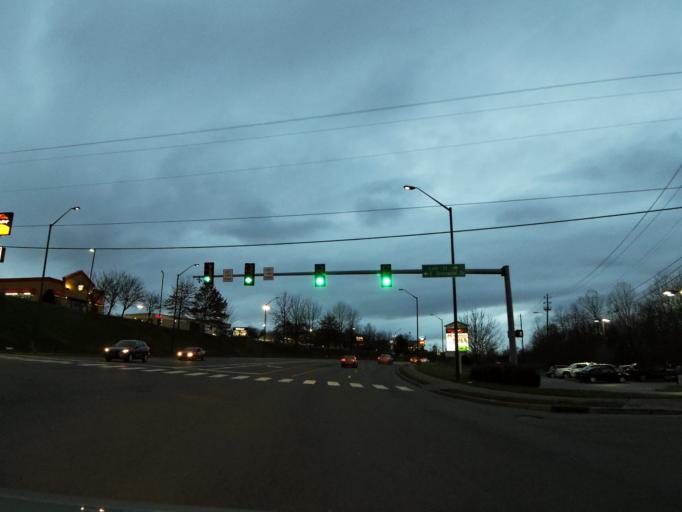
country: US
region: Tennessee
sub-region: Washington County
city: Johnson City
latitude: 36.3014
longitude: -82.3783
